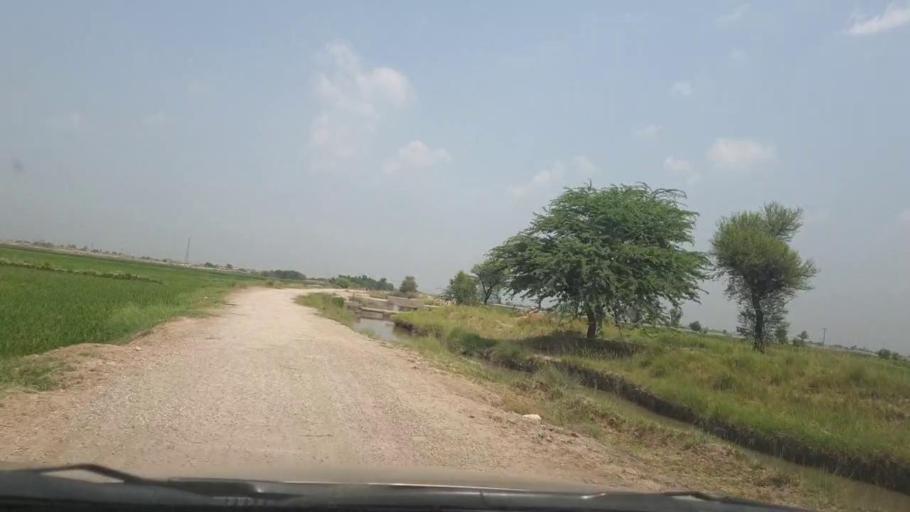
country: PK
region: Sindh
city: Ratodero
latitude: 27.6915
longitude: 68.2332
